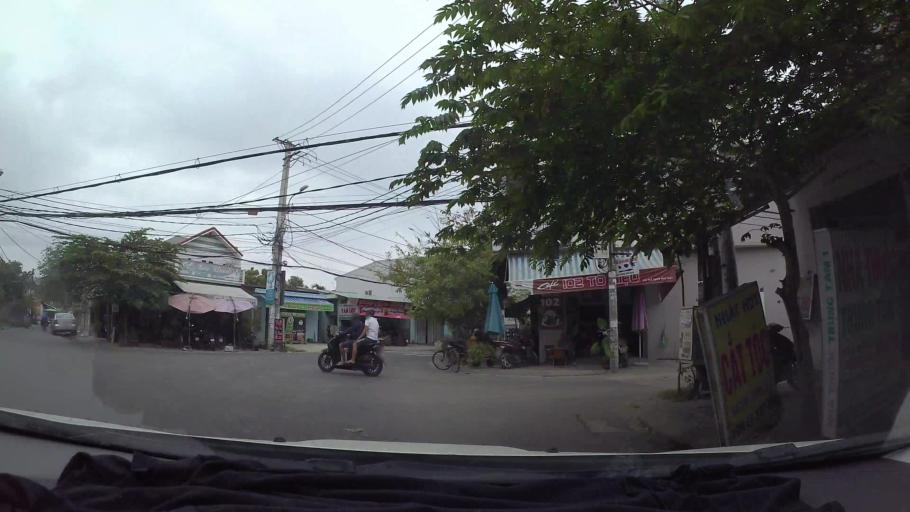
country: VN
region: Da Nang
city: Lien Chieu
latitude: 16.0603
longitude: 108.1674
